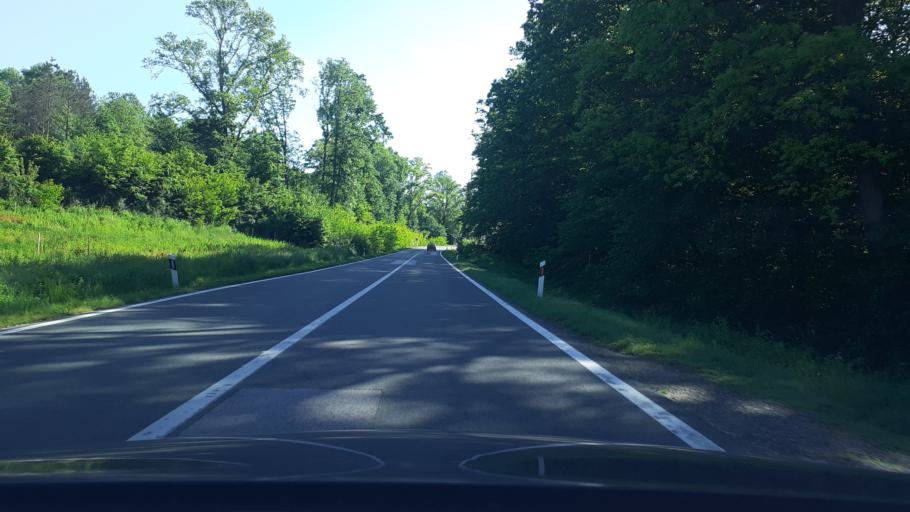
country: HR
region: Brodsko-Posavska
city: Batrina
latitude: 45.2081
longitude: 17.6826
